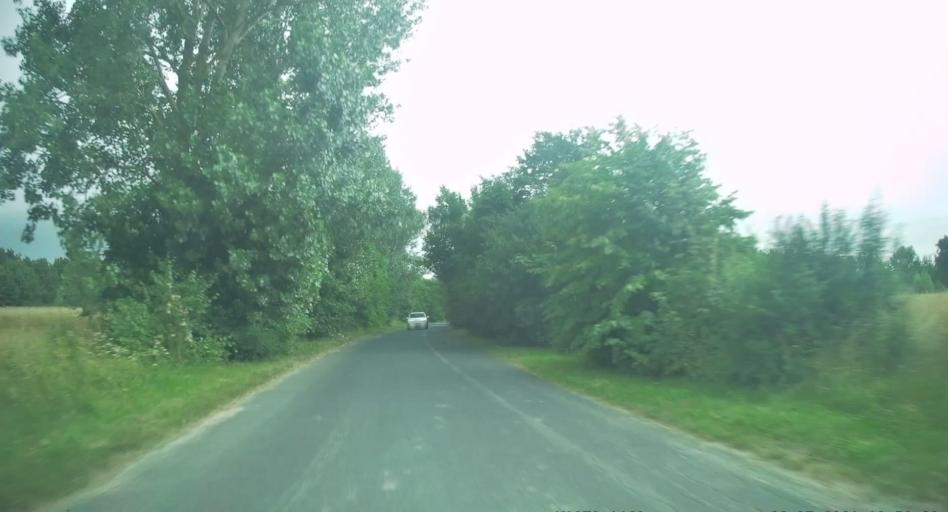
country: PL
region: Lodz Voivodeship
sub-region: Powiat rawski
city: Rawa Mazowiecka
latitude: 51.7618
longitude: 20.1864
